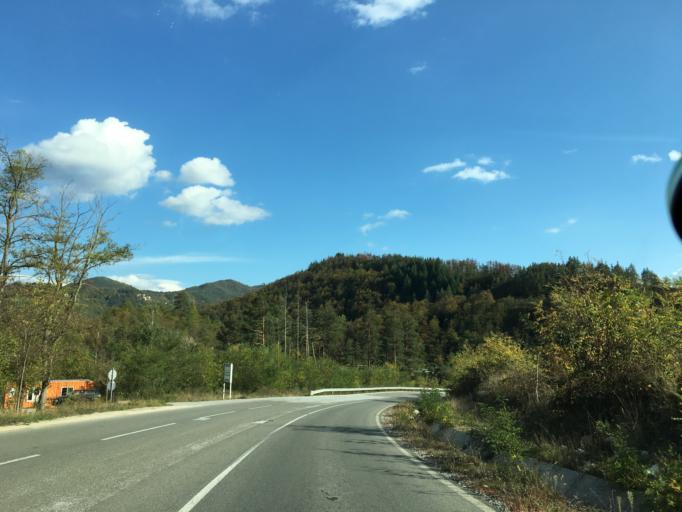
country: BG
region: Smolyan
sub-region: Obshtina Madan
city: Madan
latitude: 41.5374
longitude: 24.9188
